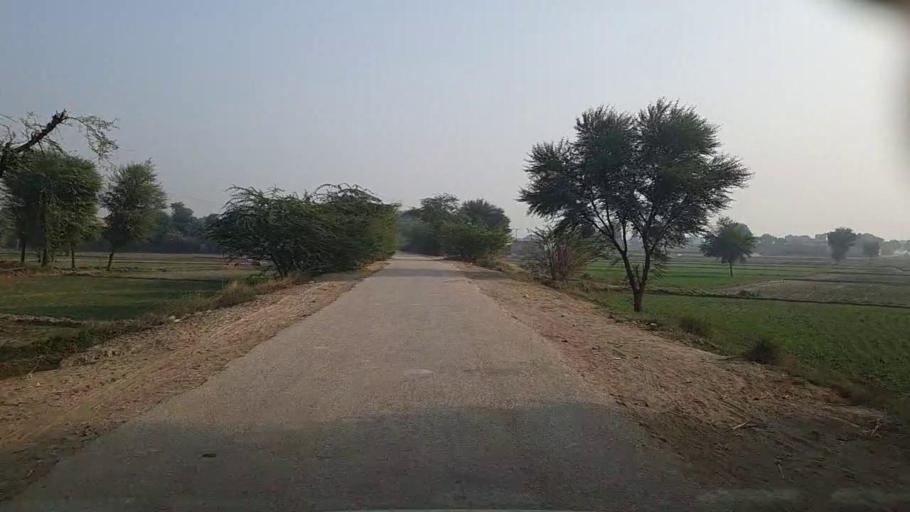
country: PK
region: Sindh
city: Kandiari
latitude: 27.0376
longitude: 68.4804
